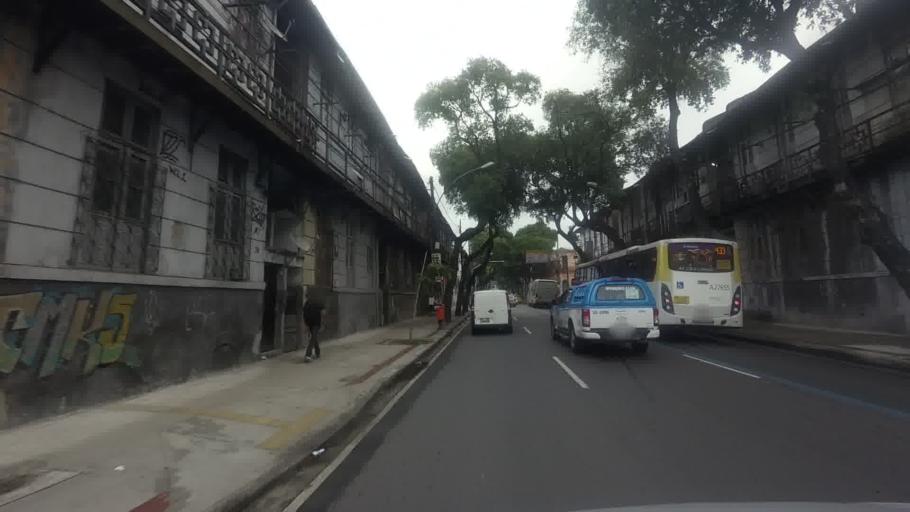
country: BR
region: Rio de Janeiro
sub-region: Rio De Janeiro
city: Rio de Janeiro
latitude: -22.9124
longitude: -43.1994
